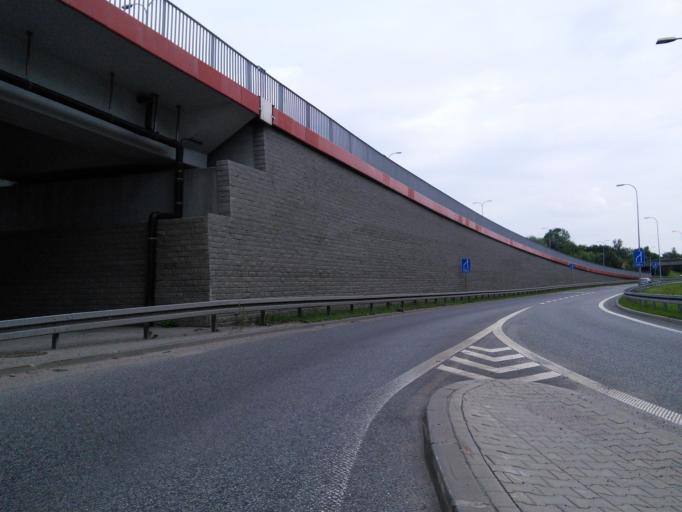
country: PL
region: Silesian Voivodeship
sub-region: Bytom
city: Bytom
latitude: 50.3654
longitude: 18.9382
